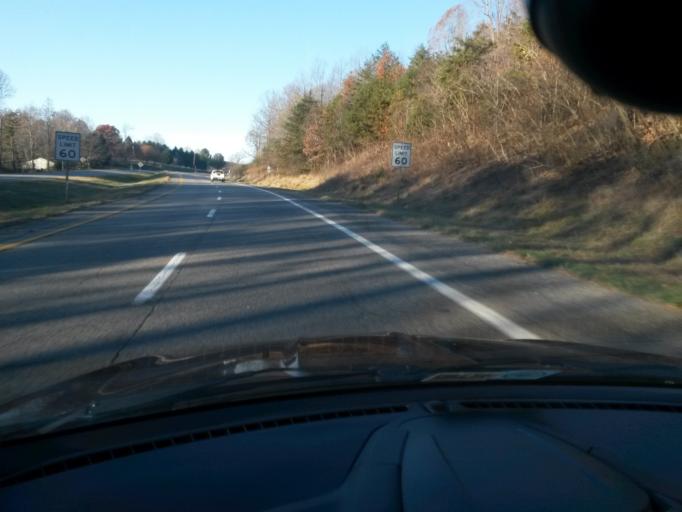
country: US
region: Virginia
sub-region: Henry County
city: Horse Pasture
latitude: 36.6252
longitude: -79.9669
